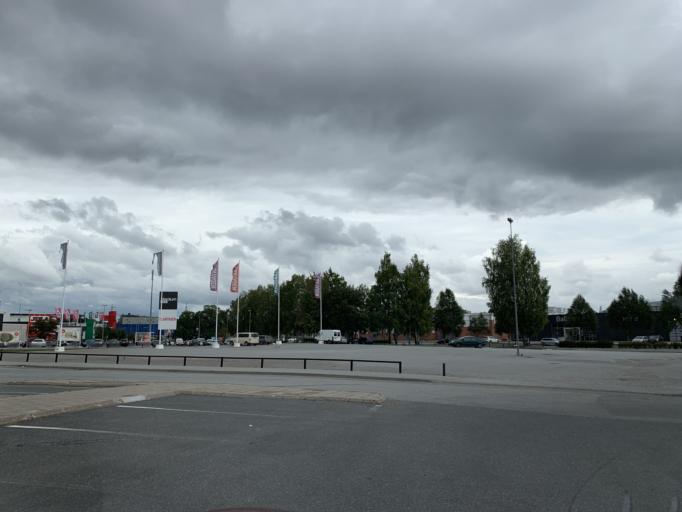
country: SE
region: Stockholm
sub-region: Huddinge Kommun
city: Segeltorp
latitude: 59.2668
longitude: 17.9213
